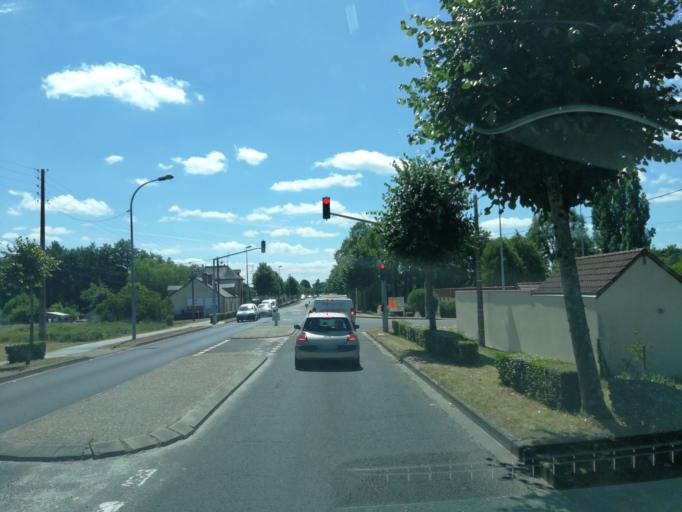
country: FR
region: Centre
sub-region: Departement du Loir-et-Cher
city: Lamotte-Beuvron
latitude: 47.6090
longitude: 2.0219
